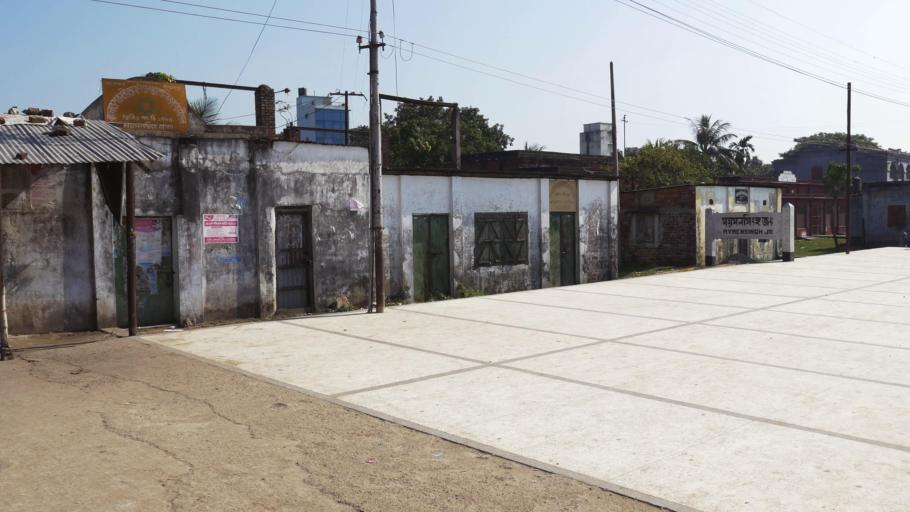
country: BD
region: Dhaka
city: Mymensingh
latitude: 24.6679
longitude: 90.4545
